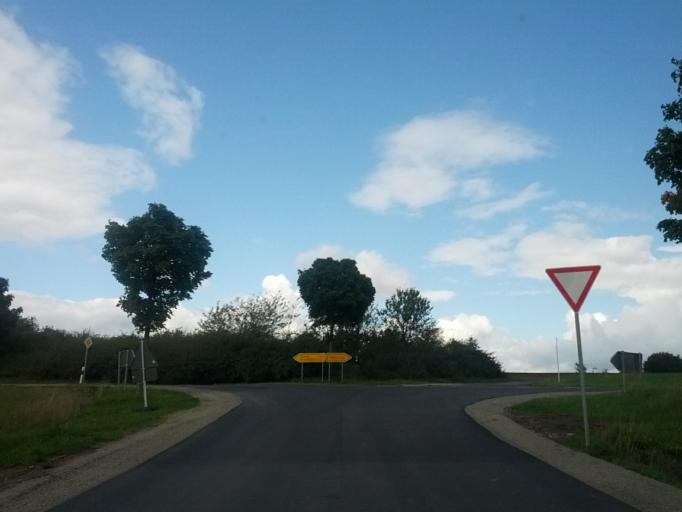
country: DE
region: Hesse
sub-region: Regierungsbezirk Kassel
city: Weissenborn
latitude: 51.0857
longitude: 10.0617
